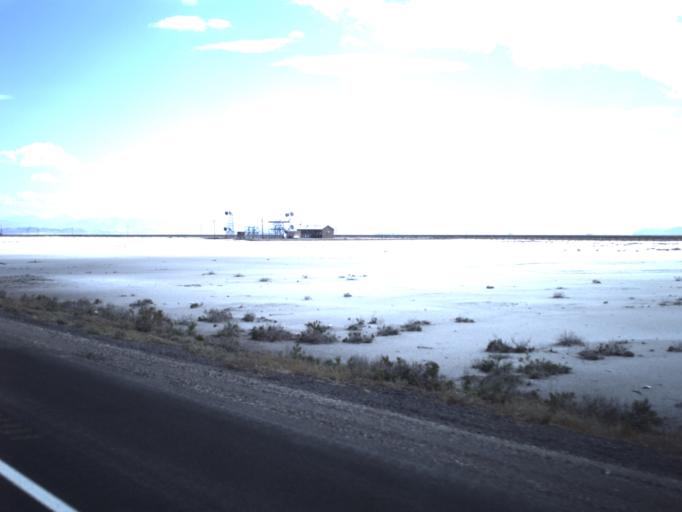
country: US
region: Utah
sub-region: Tooele County
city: Wendover
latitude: 40.7307
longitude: -113.4903
